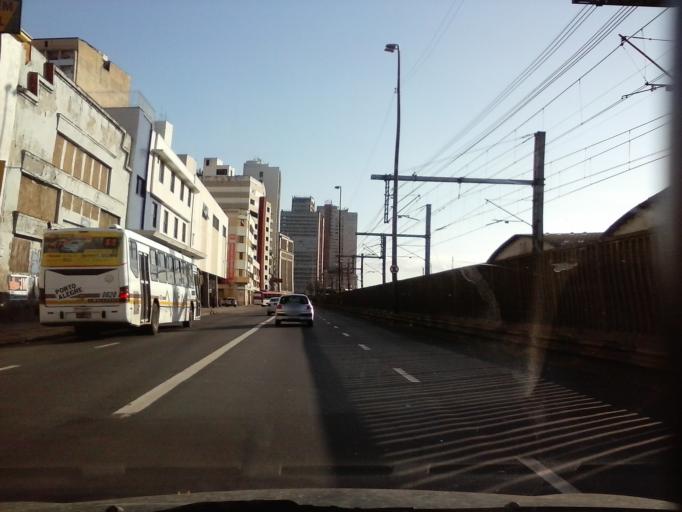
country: BR
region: Rio Grande do Sul
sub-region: Porto Alegre
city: Porto Alegre
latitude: -30.0247
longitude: -51.2241
